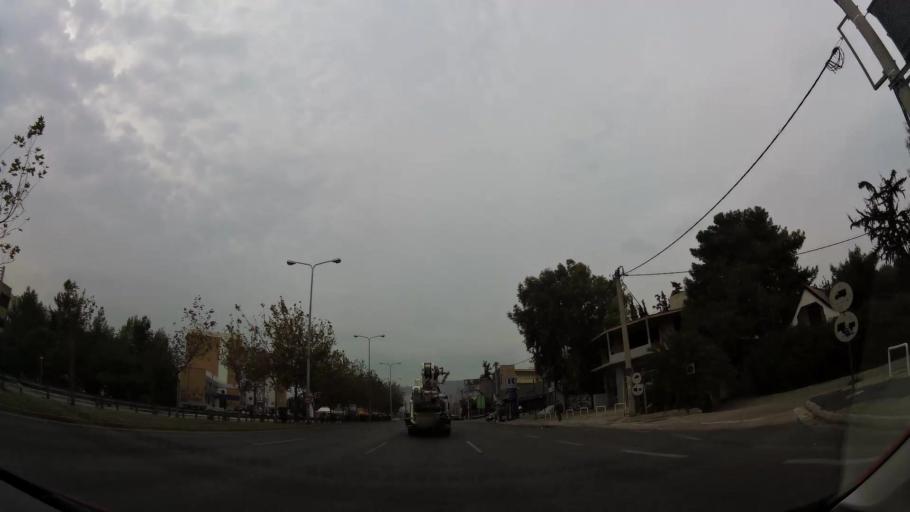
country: GR
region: Attica
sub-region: Nomarchia Athinas
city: Chaidari
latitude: 38.0086
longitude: 23.6717
